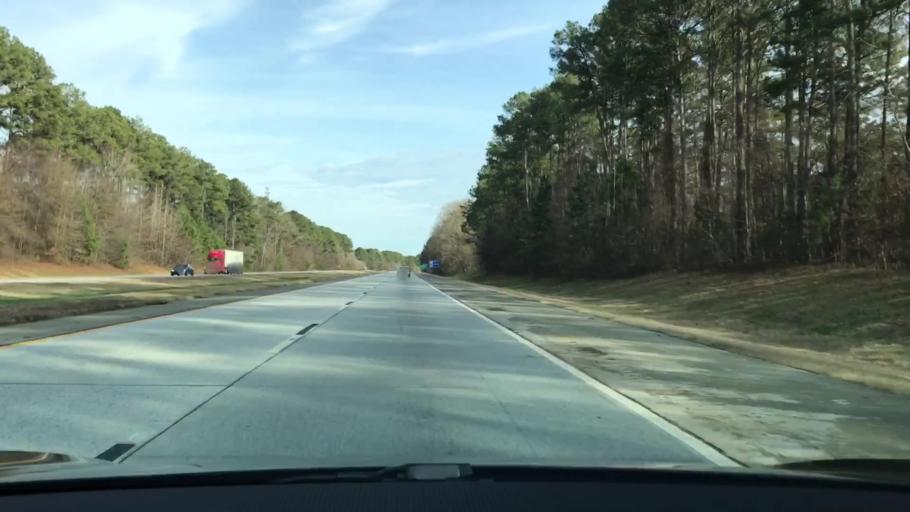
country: US
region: Georgia
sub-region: Morgan County
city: Madison
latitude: 33.5546
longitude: -83.3848
